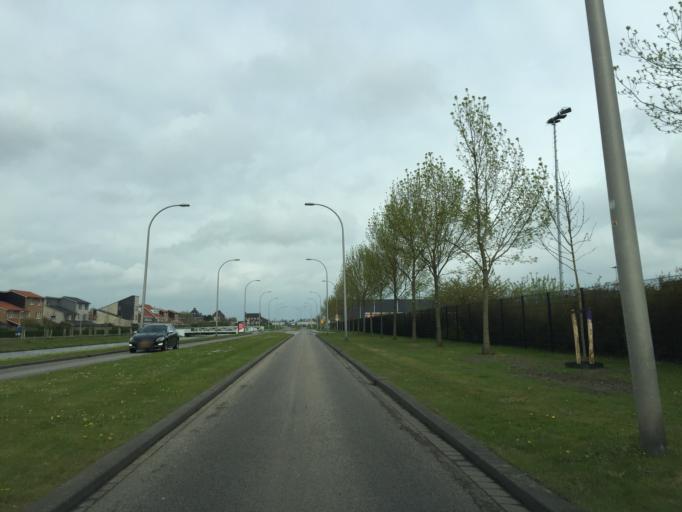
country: NL
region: South Holland
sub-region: Gemeente Den Haag
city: Ypenburg
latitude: 52.0337
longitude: 4.3865
